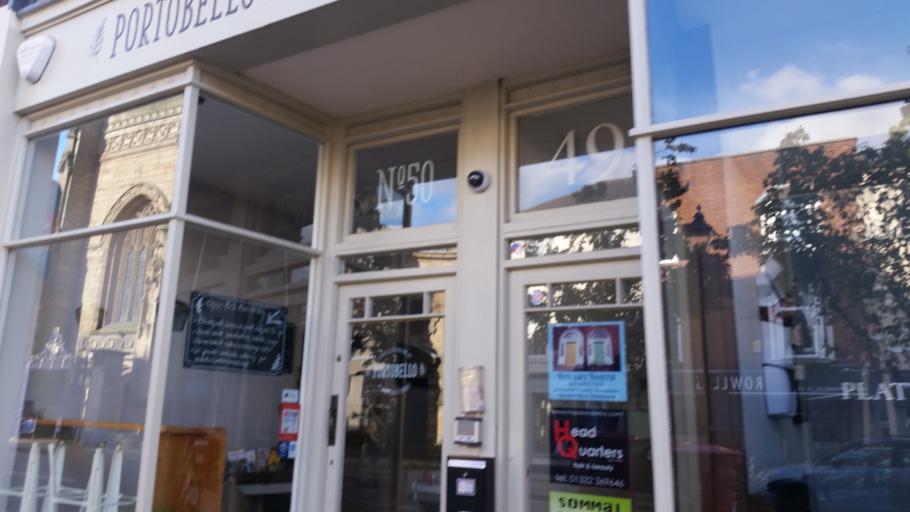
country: GB
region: England
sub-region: Derby
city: Derby
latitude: 52.9251
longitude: -1.4782
